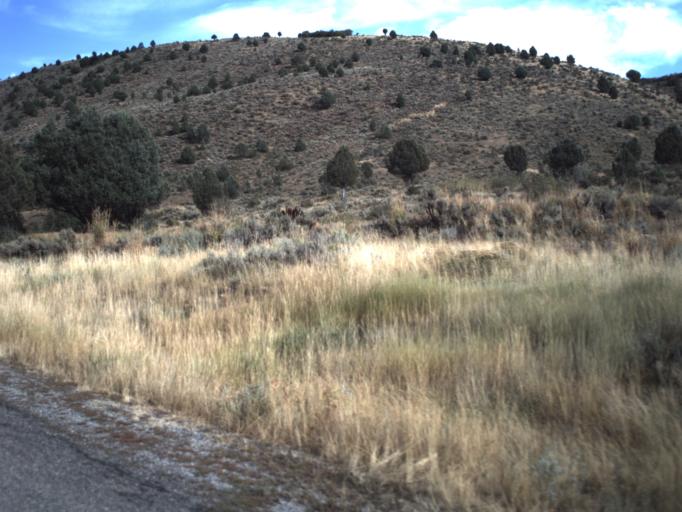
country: US
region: Utah
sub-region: Cache County
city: Millville
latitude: 41.6034
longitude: -111.5606
